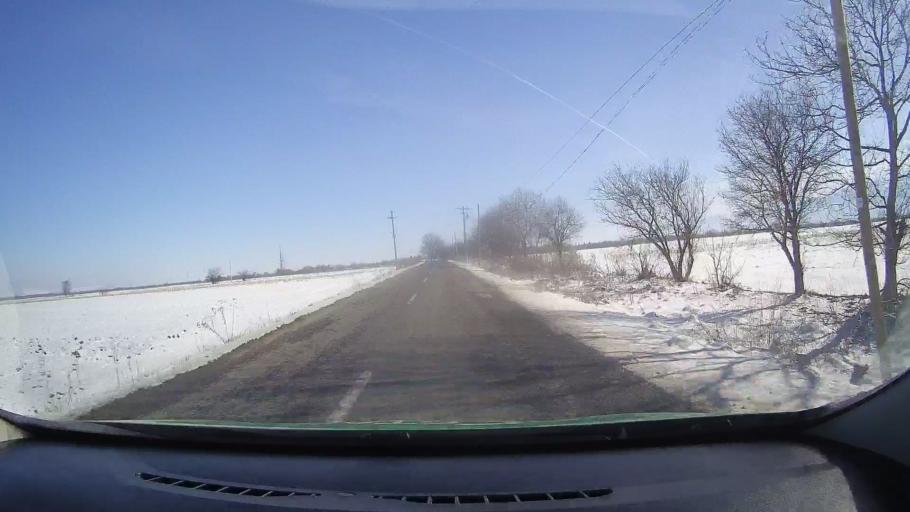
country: RO
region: Brasov
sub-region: Comuna Recea
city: Recea
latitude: 45.7326
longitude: 24.9208
